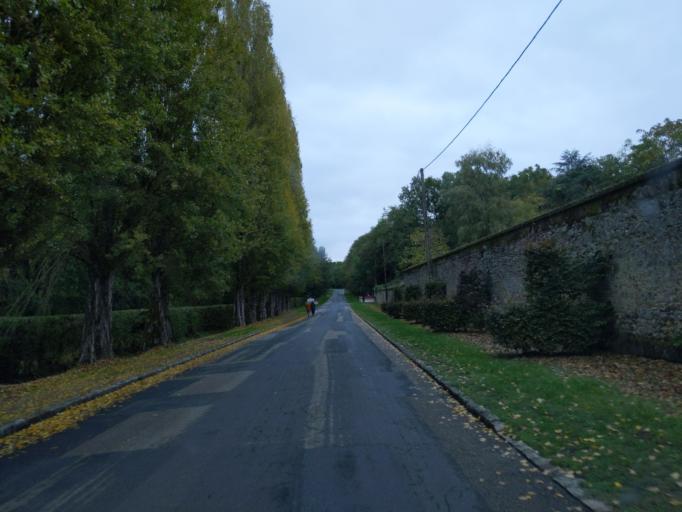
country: FR
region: Ile-de-France
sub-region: Departement des Yvelines
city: Bullion
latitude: 48.5885
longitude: 1.9900
